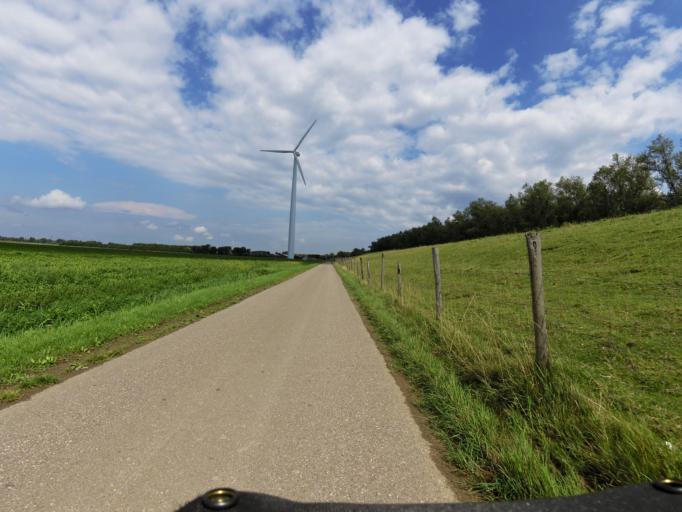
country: NL
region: South Holland
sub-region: Gemeente Strijen
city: Strijen
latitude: 51.7192
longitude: 4.6095
